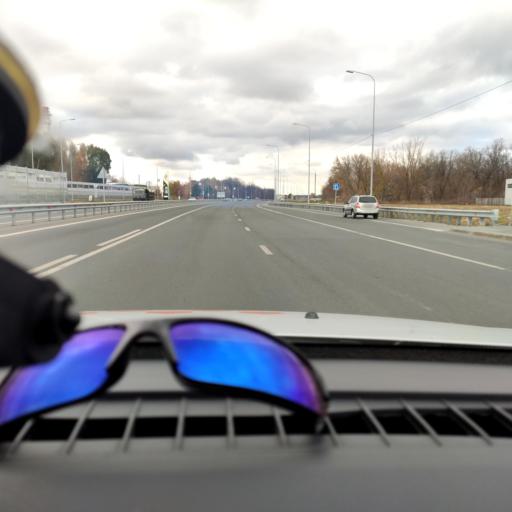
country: RU
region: Samara
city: Bereza
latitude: 53.5114
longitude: 50.1437
